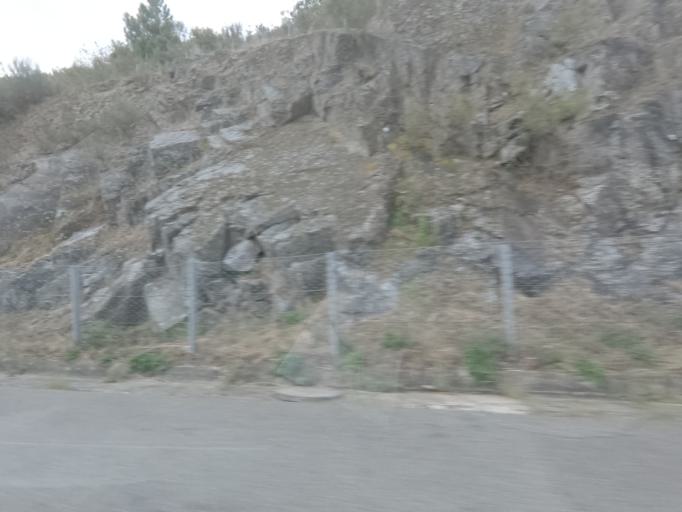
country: PT
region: Viseu
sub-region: Lamego
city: Lamego
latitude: 41.0705
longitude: -7.8268
